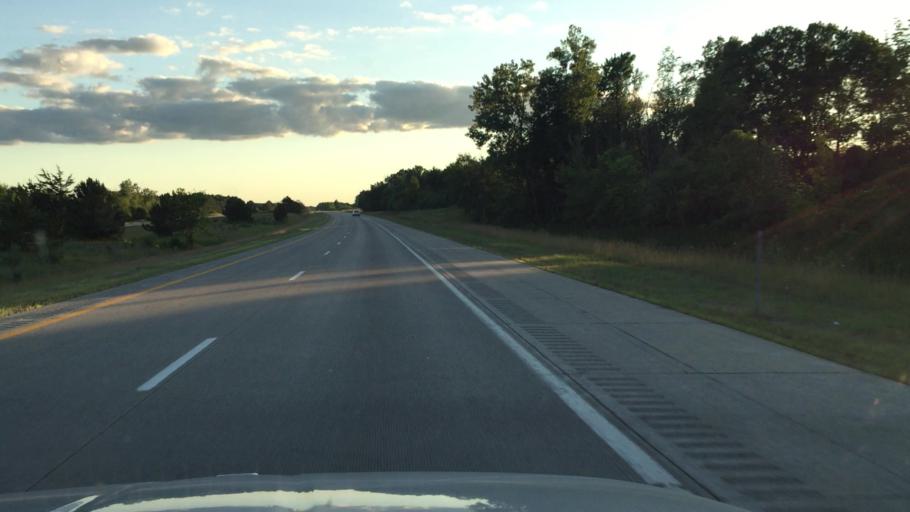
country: US
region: Michigan
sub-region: Lapeer County
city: Lapeer
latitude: 43.0282
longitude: -83.3885
